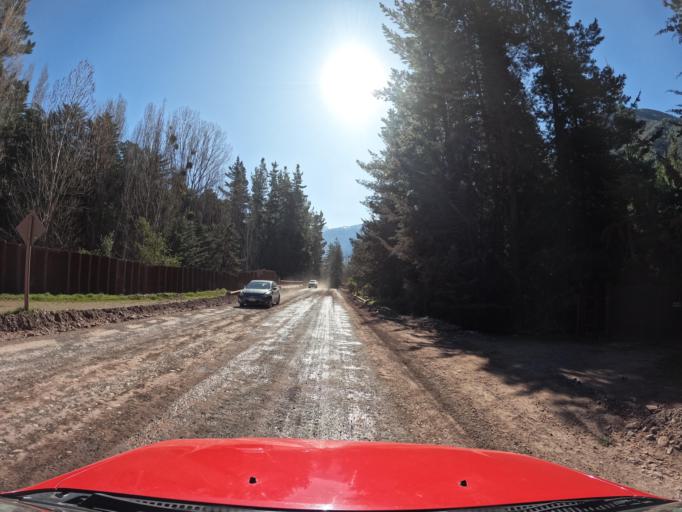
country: CL
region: O'Higgins
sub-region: Provincia de Colchagua
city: Chimbarongo
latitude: -35.0092
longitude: -70.7483
